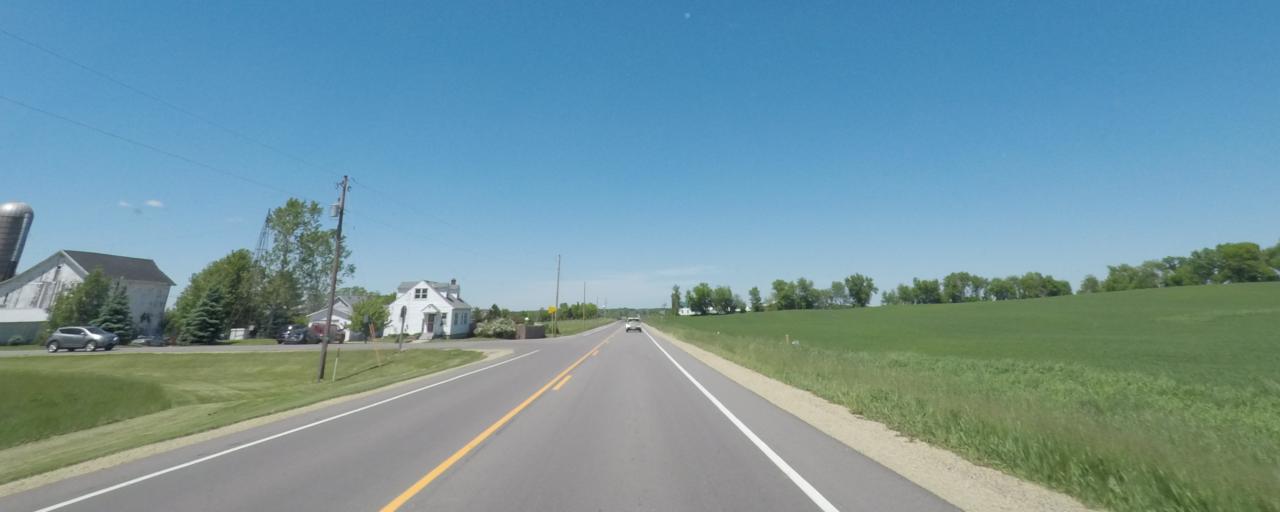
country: US
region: Wisconsin
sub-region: Green County
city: Brooklyn
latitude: 42.8275
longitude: -89.3693
